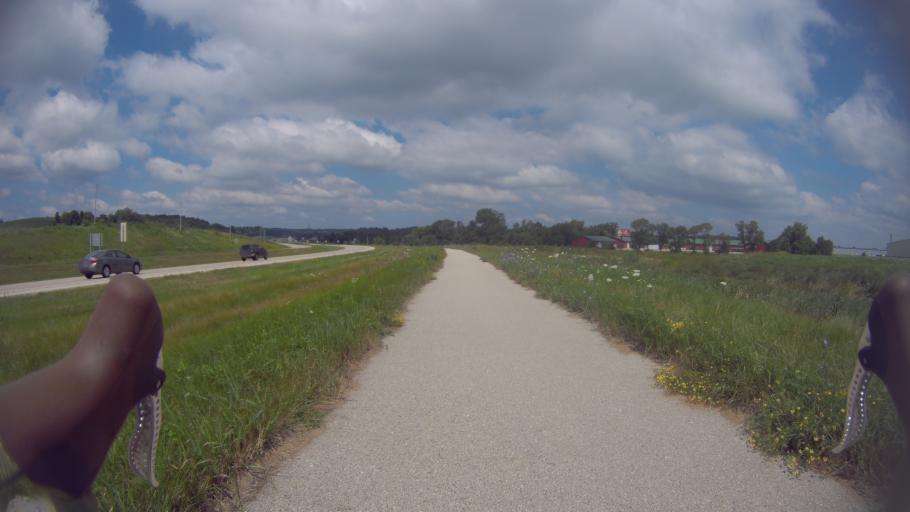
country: US
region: Wisconsin
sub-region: Dane County
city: Waunakee
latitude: 43.1894
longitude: -89.5575
